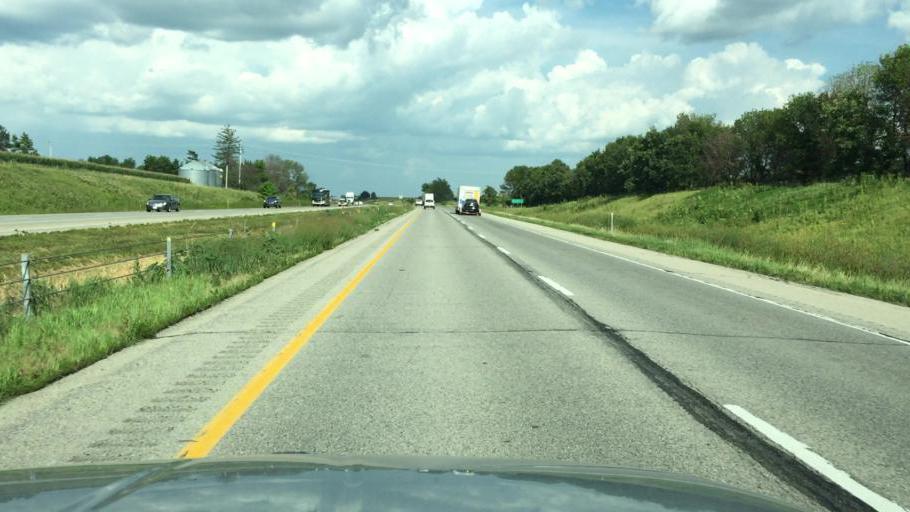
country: US
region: Iowa
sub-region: Poweshiek County
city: Grinnell
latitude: 41.6952
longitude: -92.7114
